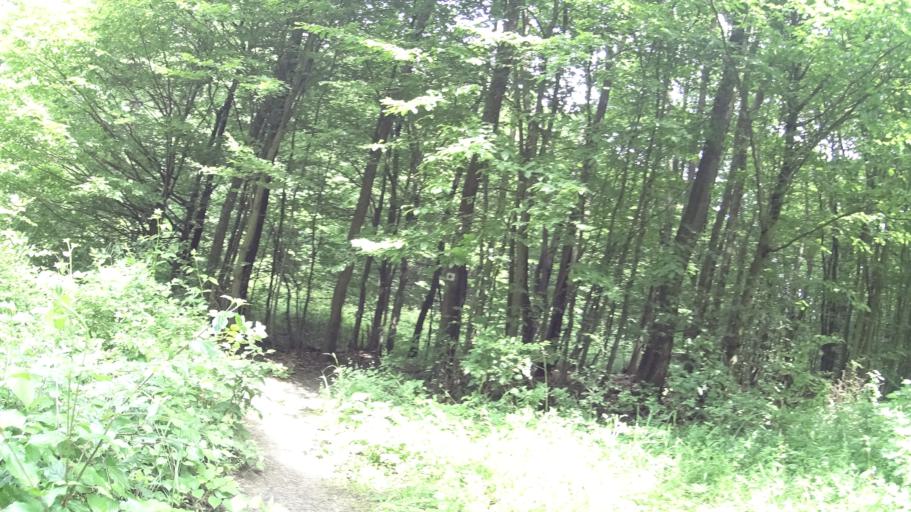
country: HU
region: Pest
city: Nagymaros
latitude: 47.8011
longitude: 18.9291
